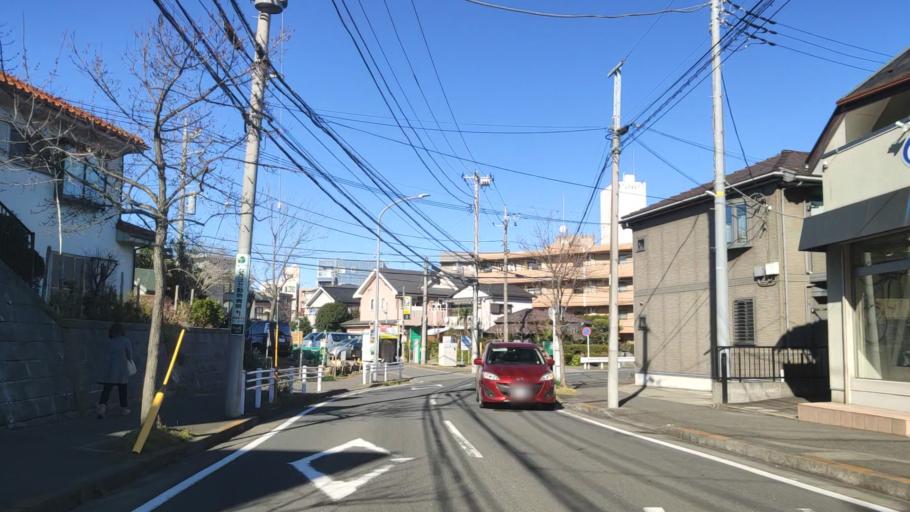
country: JP
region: Tokyo
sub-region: Machida-shi
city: Machida
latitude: 35.5122
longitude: 139.5370
